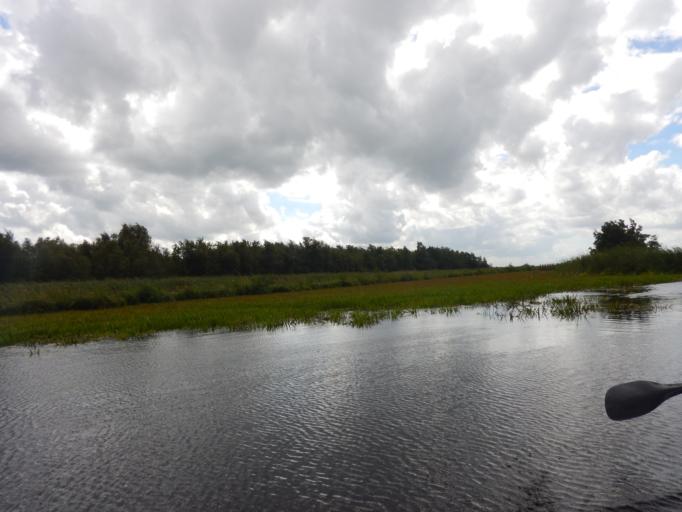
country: NL
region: Overijssel
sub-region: Gemeente Steenwijkerland
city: Blokzijl
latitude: 52.7706
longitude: 5.9488
